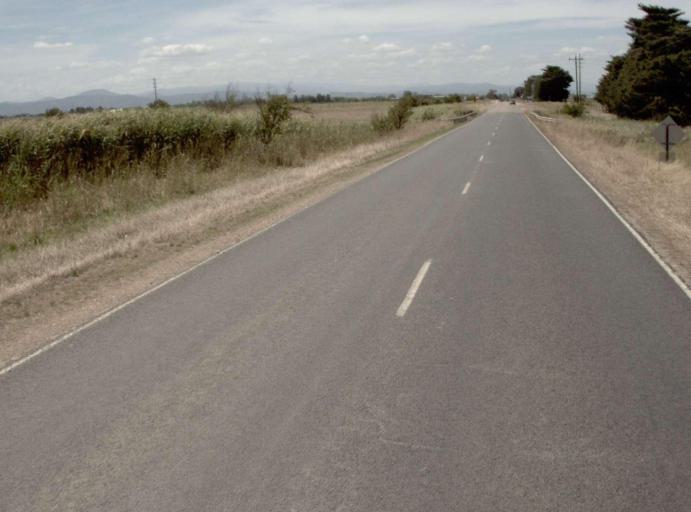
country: AU
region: Victoria
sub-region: Wellington
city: Heyfield
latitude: -37.9938
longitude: 146.8857
